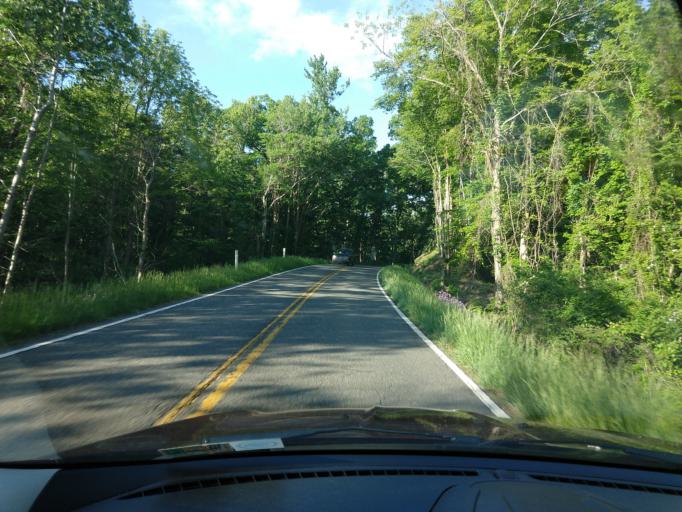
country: US
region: Virginia
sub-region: City of Galax
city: Galax
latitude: 36.8187
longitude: -80.9608
